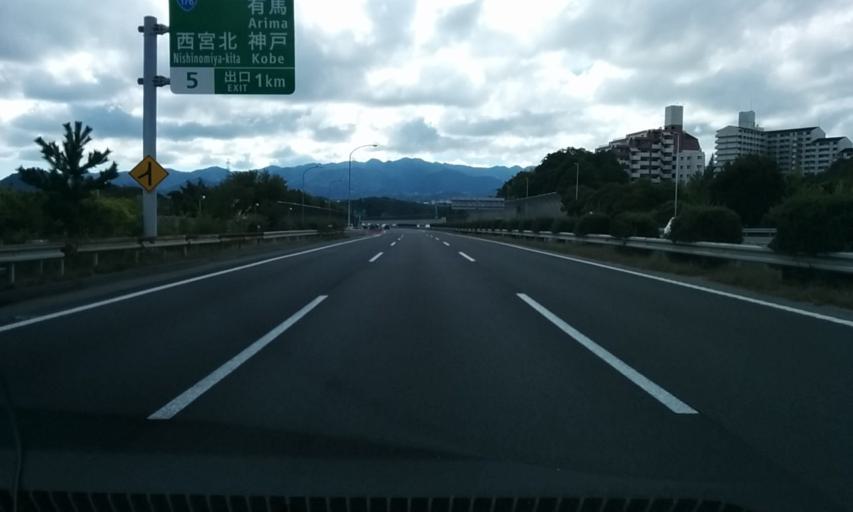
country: JP
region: Hyogo
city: Sandacho
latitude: 34.8460
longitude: 135.2252
